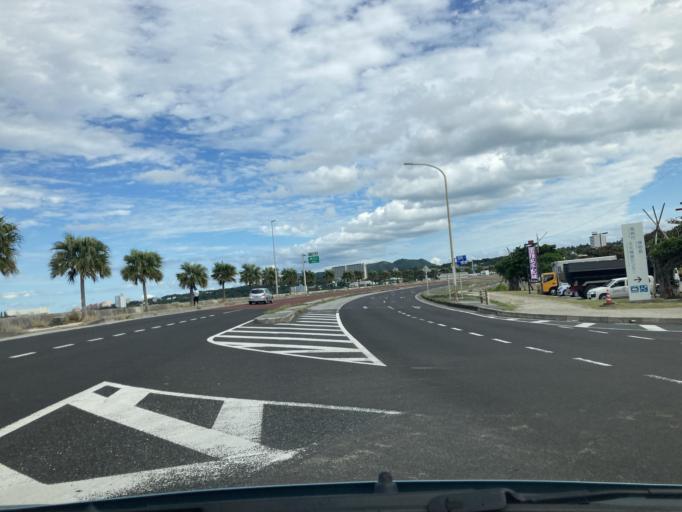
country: JP
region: Okinawa
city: Ishikawa
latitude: 26.4369
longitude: 127.7916
